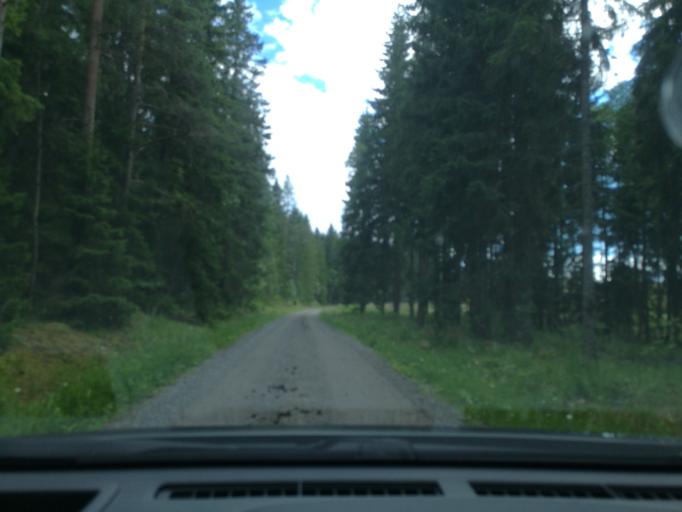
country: SE
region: Vaestmanland
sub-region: Surahammars Kommun
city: Ramnas
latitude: 59.8048
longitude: 16.3086
